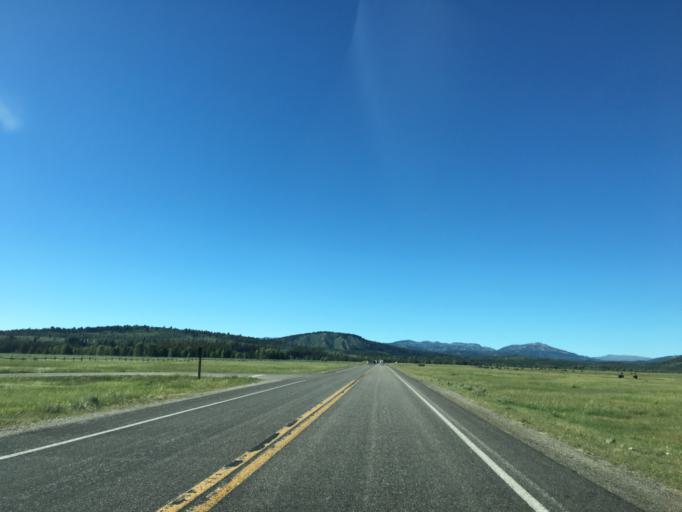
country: US
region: Wyoming
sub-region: Teton County
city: Jackson
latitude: 43.8107
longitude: -110.5266
